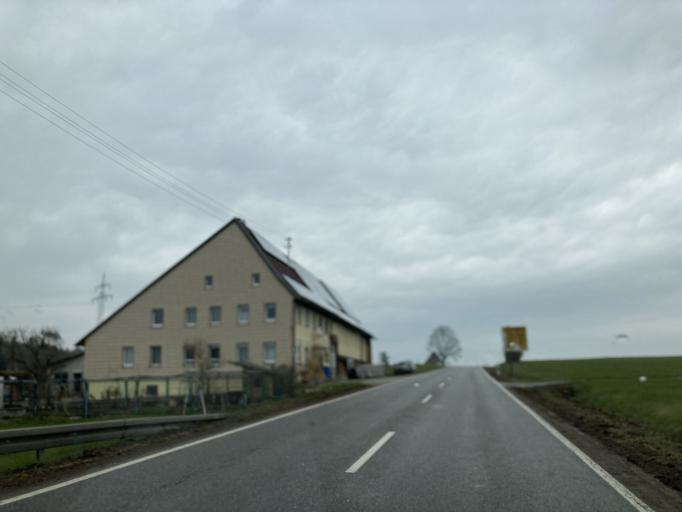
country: DE
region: Baden-Wuerttemberg
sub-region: Freiburg Region
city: Seedorf
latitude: 48.2596
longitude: 8.4572
